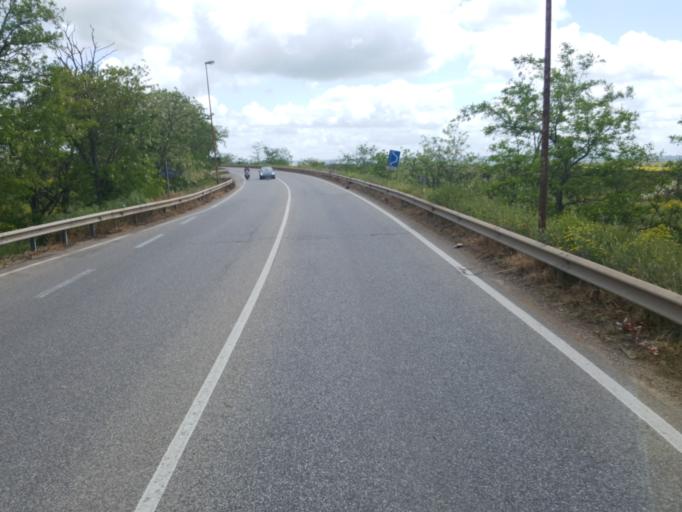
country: IT
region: Apulia
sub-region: Provincia di Bari
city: Altamura
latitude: 40.8145
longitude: 16.5567
